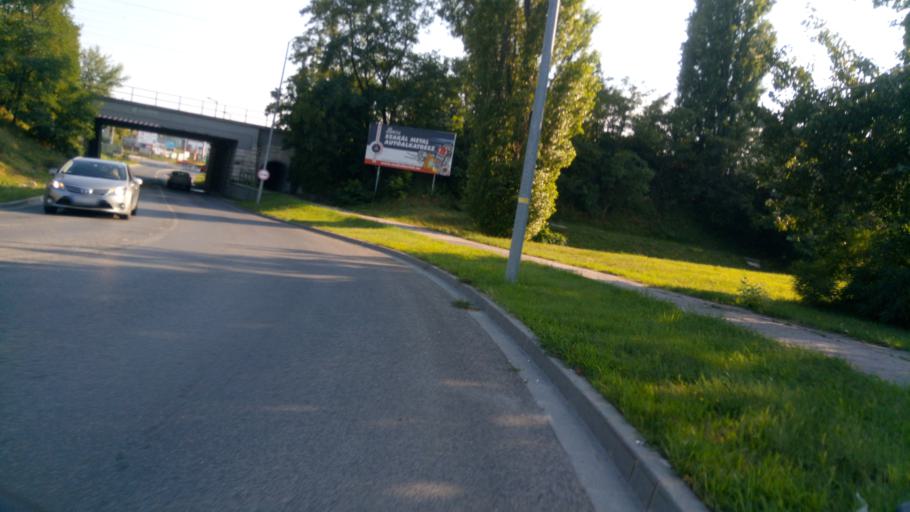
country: HU
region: Pest
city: Budaors
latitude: 47.4478
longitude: 18.9757
